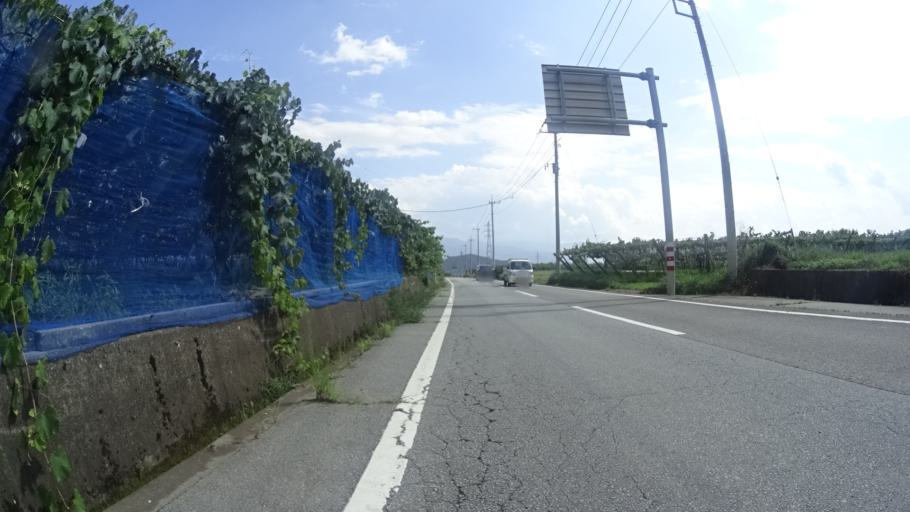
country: JP
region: Yamanashi
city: Enzan
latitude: 35.7372
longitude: 138.7214
